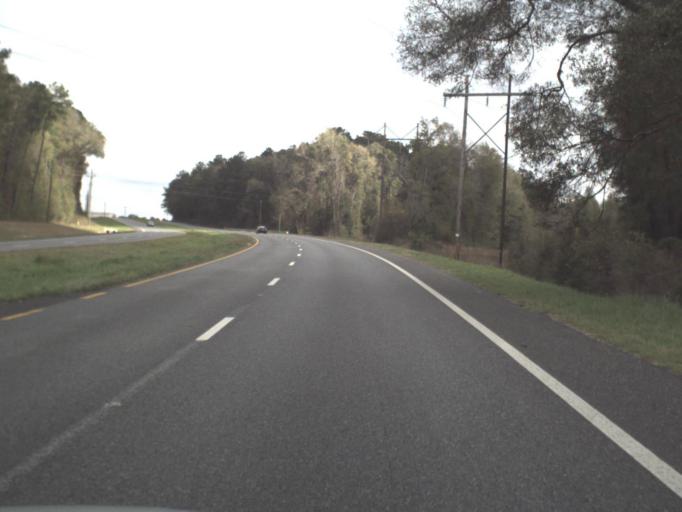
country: US
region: Florida
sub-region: Gadsden County
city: Havana
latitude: 30.5515
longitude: -84.3824
